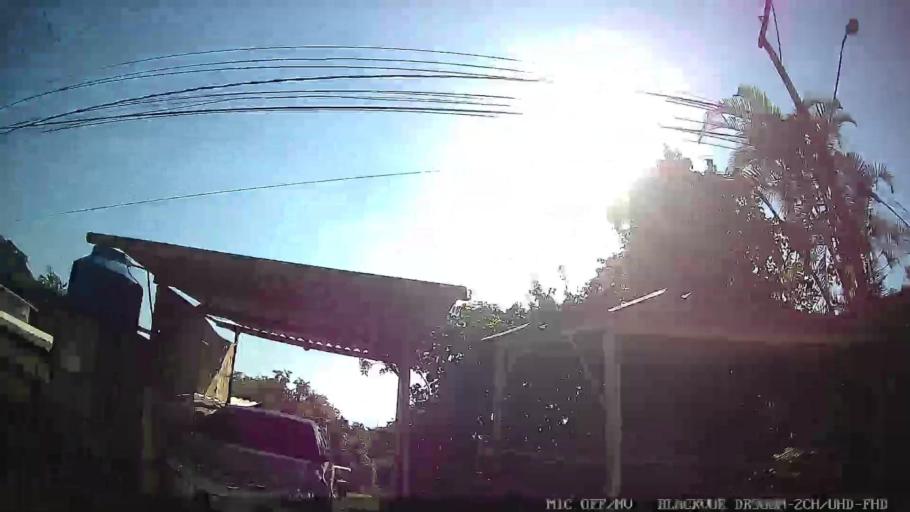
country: BR
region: Sao Paulo
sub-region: Guaruja
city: Guaruja
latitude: -24.0101
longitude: -46.2820
